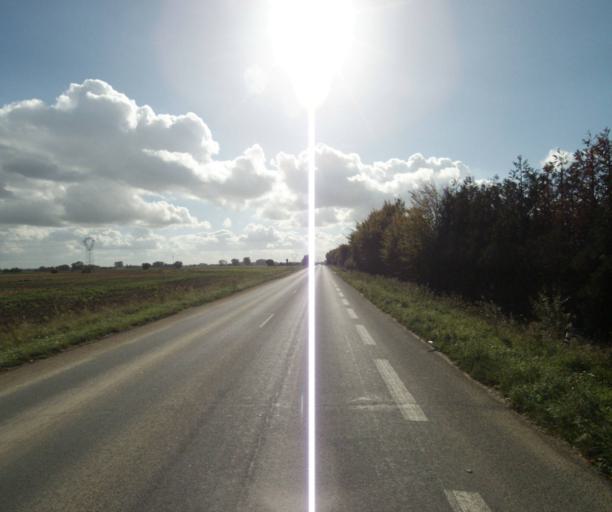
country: FR
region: Nord-Pas-de-Calais
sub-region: Departement du Nord
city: Frelinghien
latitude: 50.7089
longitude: 2.9380
